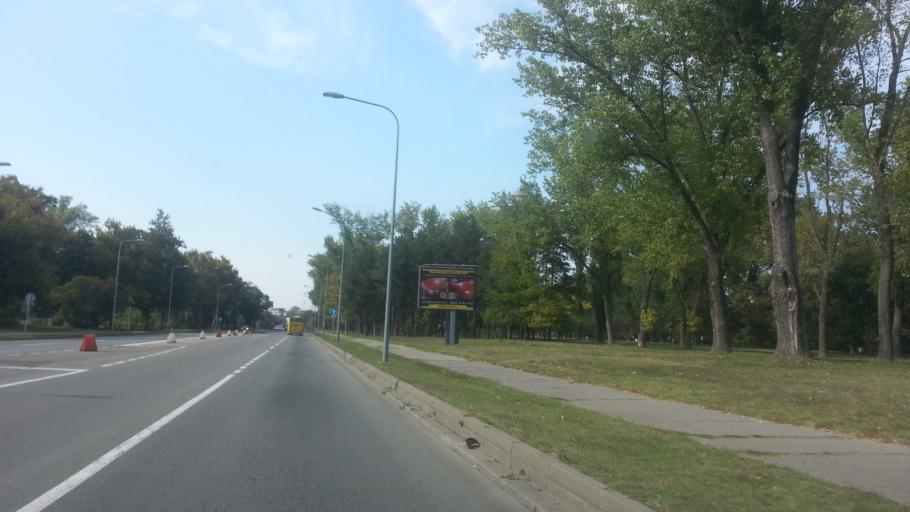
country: RS
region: Central Serbia
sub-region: Belgrade
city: Novi Beograd
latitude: 44.8218
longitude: 20.4284
